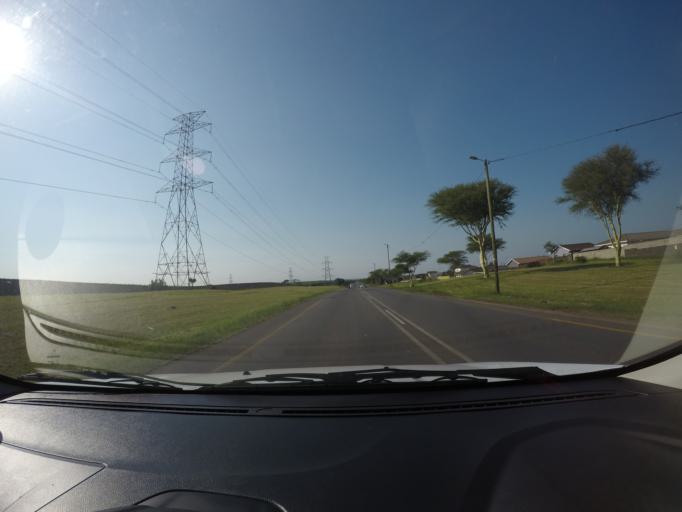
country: ZA
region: KwaZulu-Natal
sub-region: uThungulu District Municipality
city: Richards Bay
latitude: -28.7275
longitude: 32.0364
